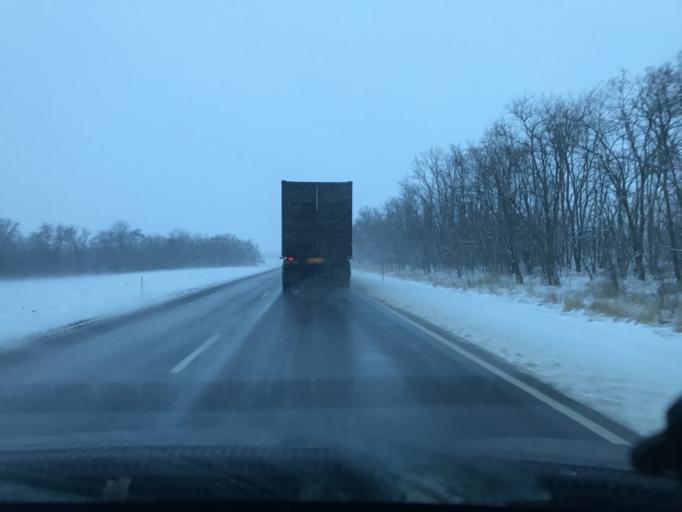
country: RU
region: Rostov
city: Letnik
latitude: 46.0758
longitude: 41.1970
